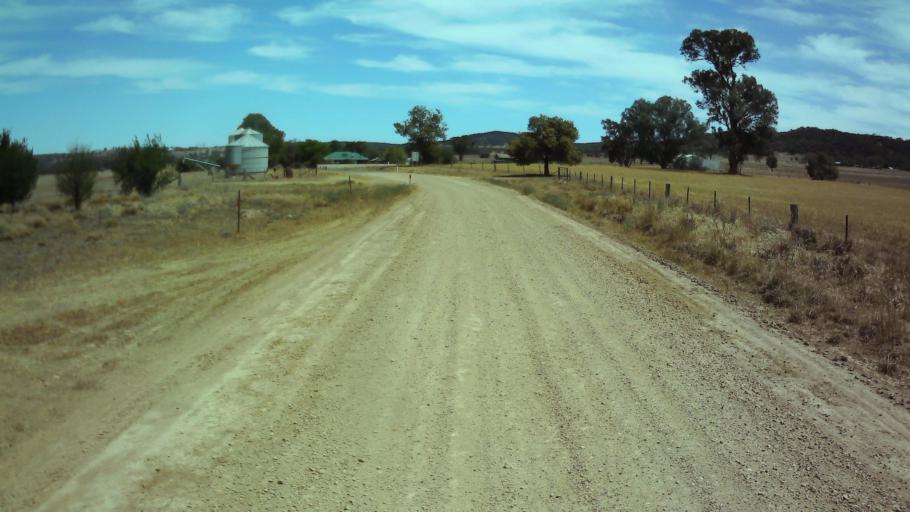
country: AU
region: New South Wales
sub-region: Weddin
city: Grenfell
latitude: -33.8313
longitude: 148.1748
